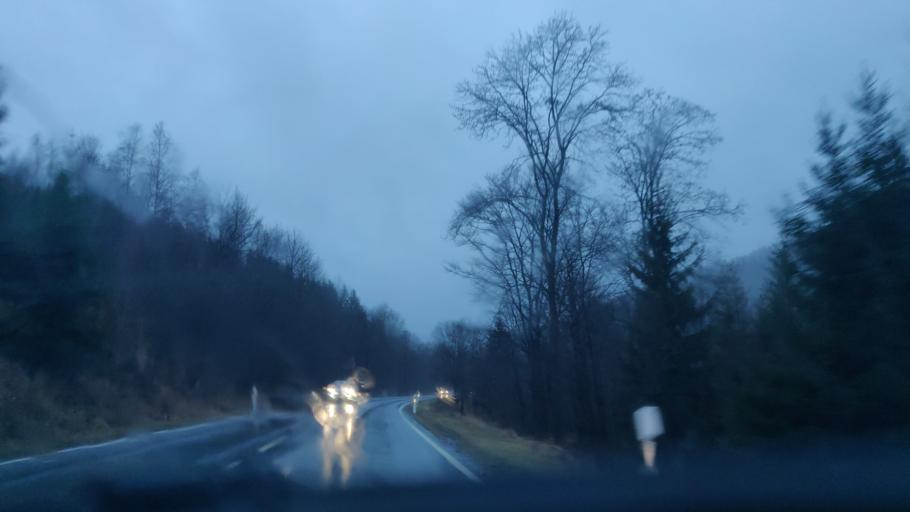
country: DE
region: Lower Saxony
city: Wieda
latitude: 51.6836
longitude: 10.5744
